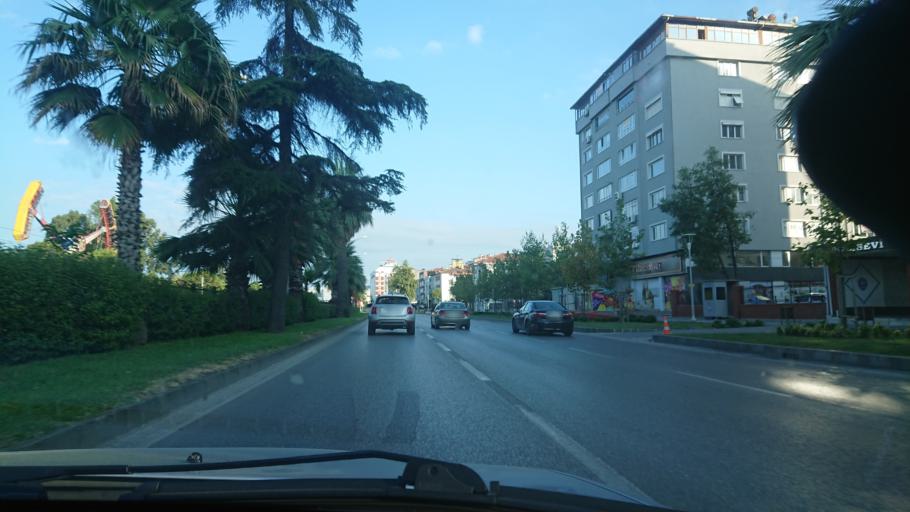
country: TR
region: Samsun
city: Samsun
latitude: 41.2877
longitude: 36.3389
